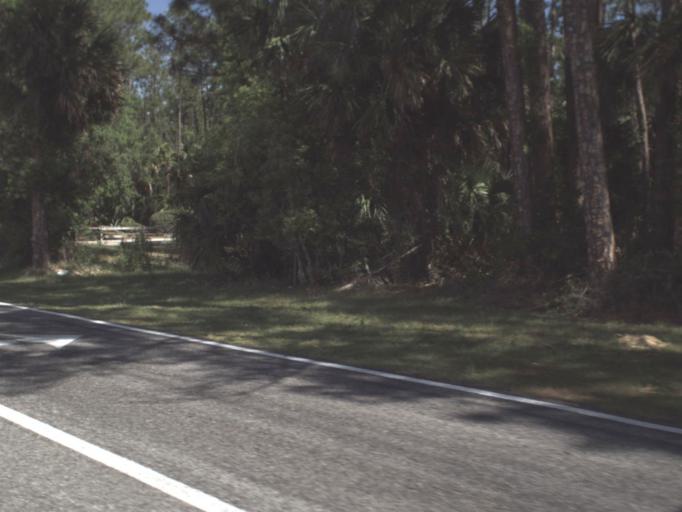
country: US
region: Florida
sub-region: Volusia County
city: Ormond-by-the-Sea
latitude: 29.3589
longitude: -81.1622
